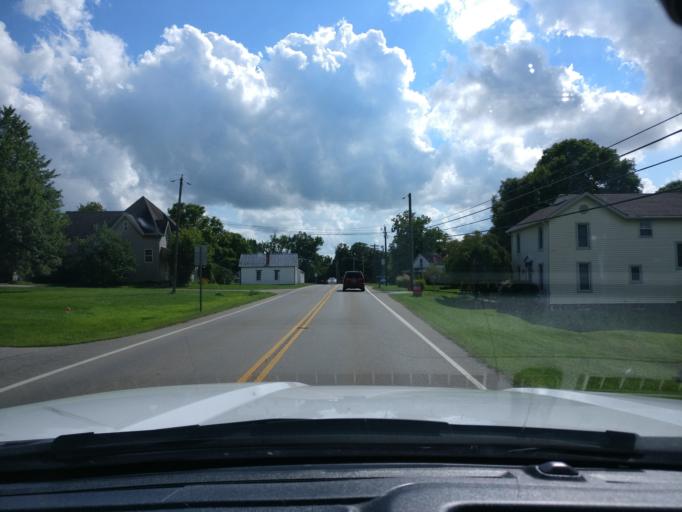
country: US
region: Ohio
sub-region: Warren County
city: Five Points
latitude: 39.5308
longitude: -84.1755
